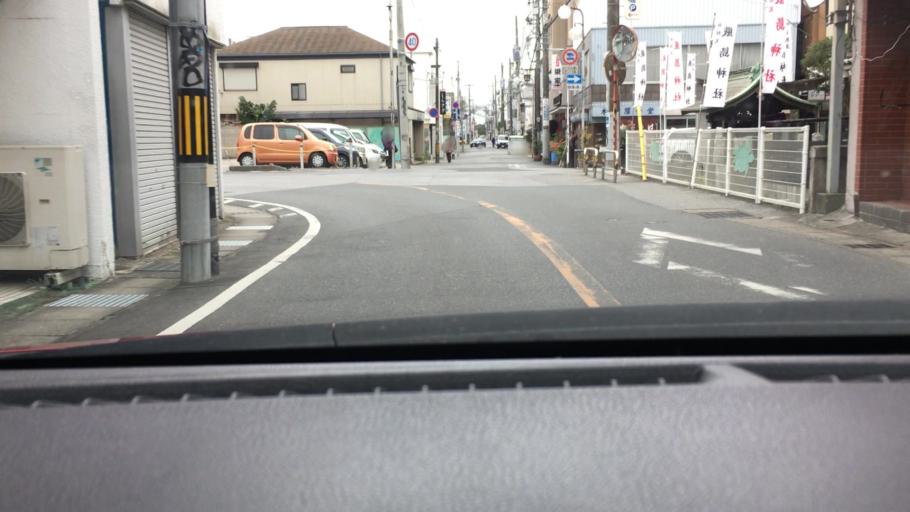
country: JP
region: Chiba
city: Kisarazu
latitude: 35.3811
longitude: 139.9225
